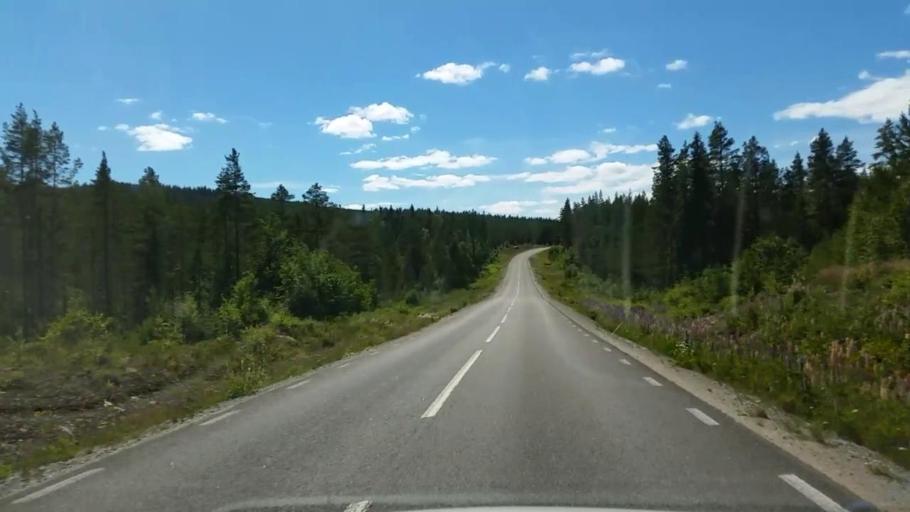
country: SE
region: Gaevleborg
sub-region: Ljusdals Kommun
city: Farila
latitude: 61.6312
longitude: 15.5778
